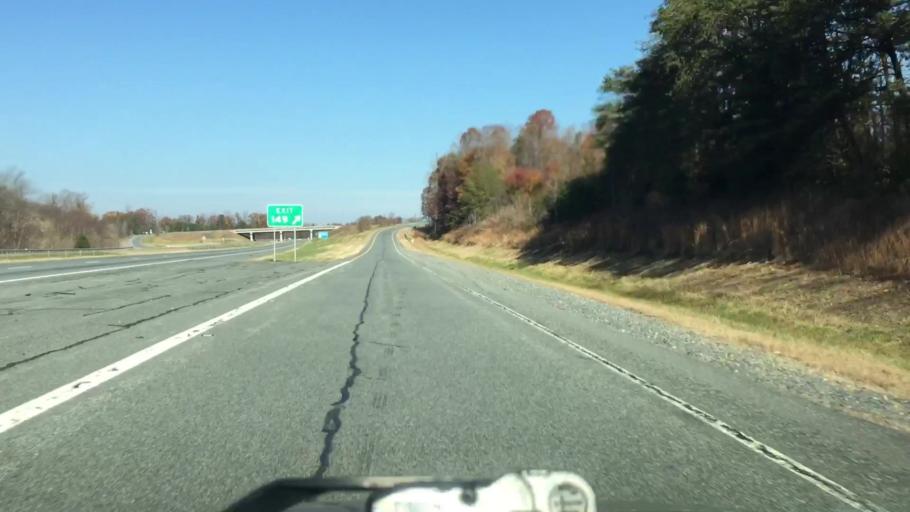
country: US
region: North Carolina
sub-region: Rockingham County
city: Reidsville
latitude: 36.3067
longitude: -79.6429
